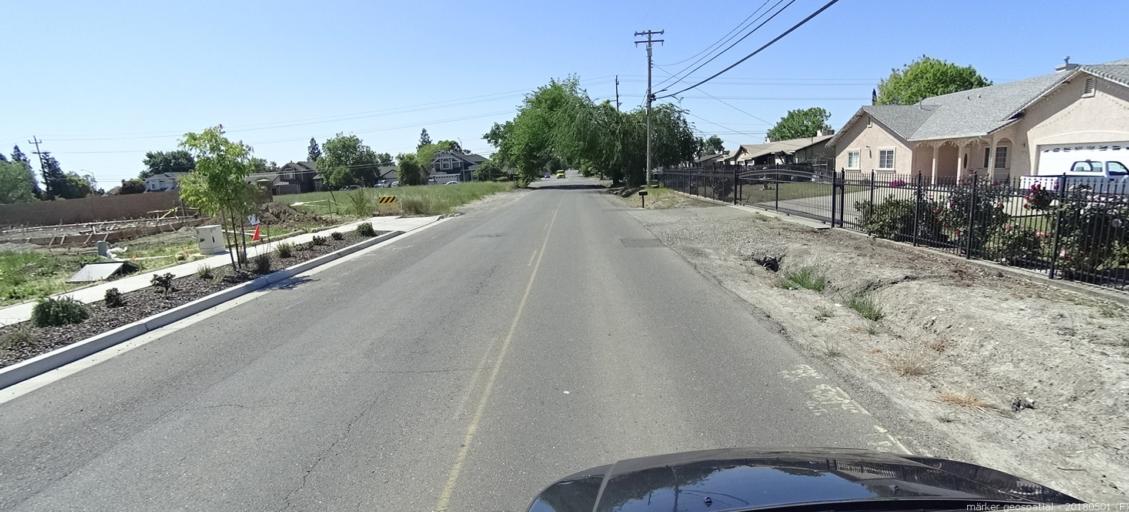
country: US
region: California
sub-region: Sacramento County
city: Rio Linda
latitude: 38.6484
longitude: -121.4384
